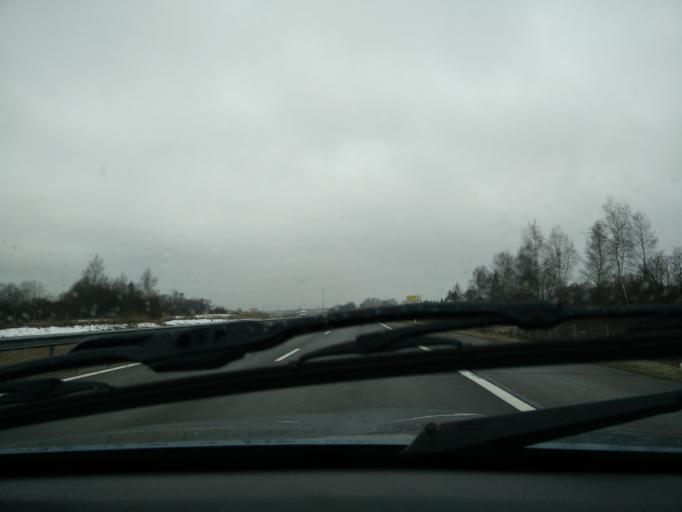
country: LT
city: Silale
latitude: 55.5536
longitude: 22.2575
